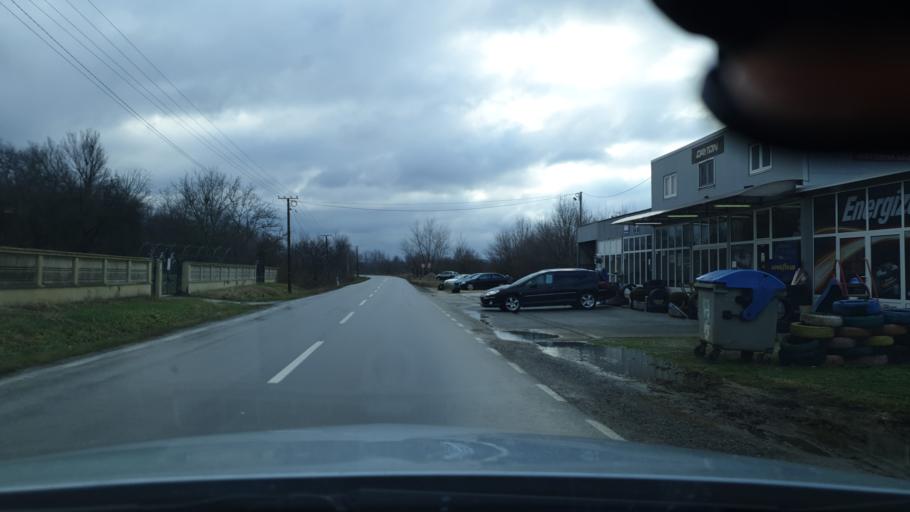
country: RS
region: Central Serbia
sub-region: Branicevski Okrug
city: Petrovac
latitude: 44.4425
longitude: 21.3435
